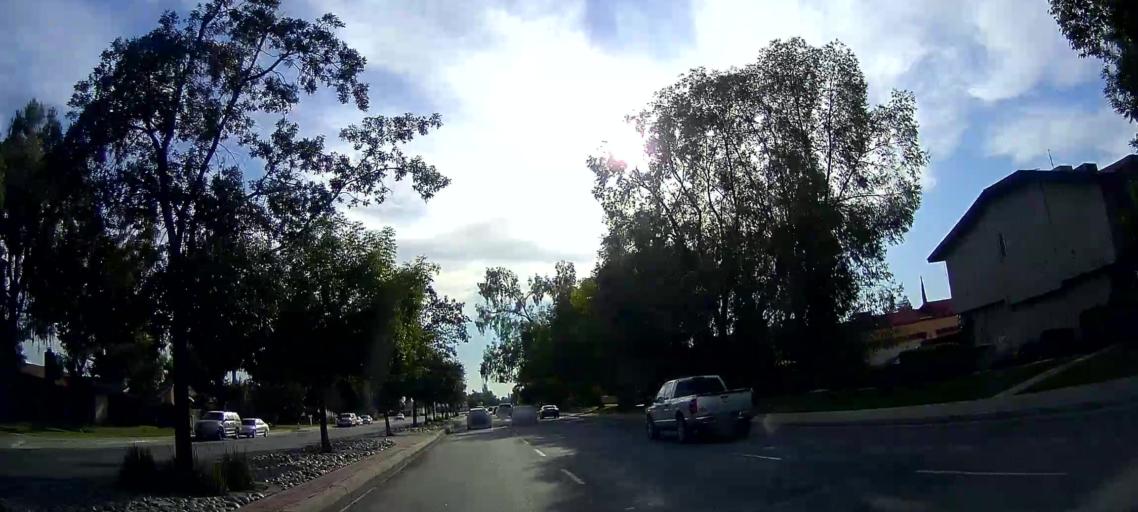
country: US
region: California
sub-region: Kern County
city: Bakersfield
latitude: 35.3178
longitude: -119.0498
